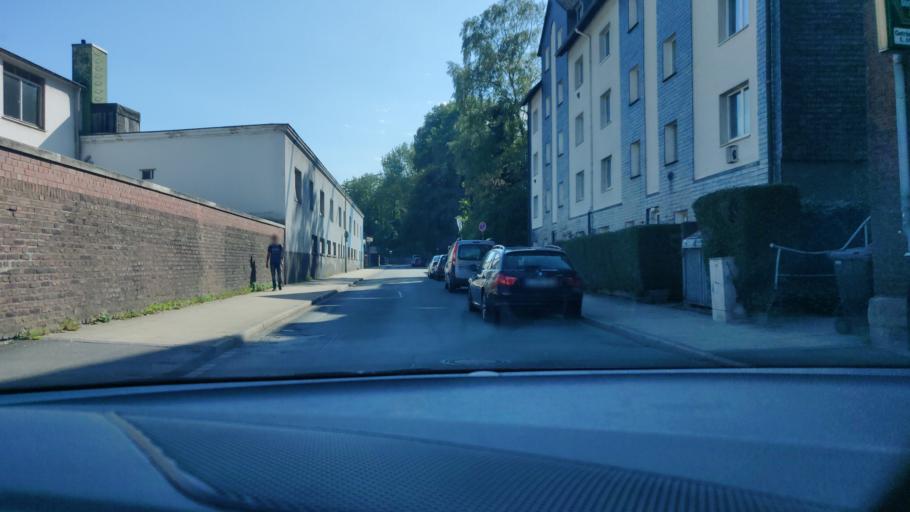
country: DE
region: North Rhine-Westphalia
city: Hattingen
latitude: 51.3579
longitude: 7.1213
